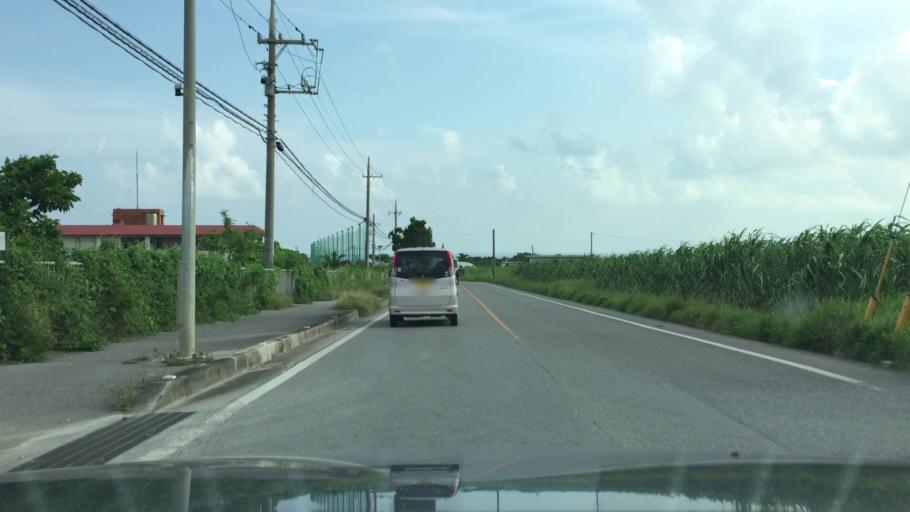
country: JP
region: Okinawa
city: Ishigaki
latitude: 24.3598
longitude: 124.1743
